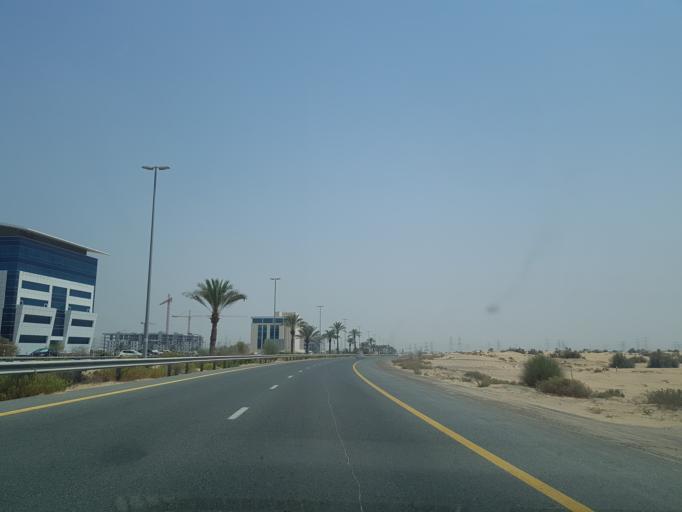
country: AE
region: Ash Shariqah
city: Sharjah
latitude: 25.1237
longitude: 55.4273
